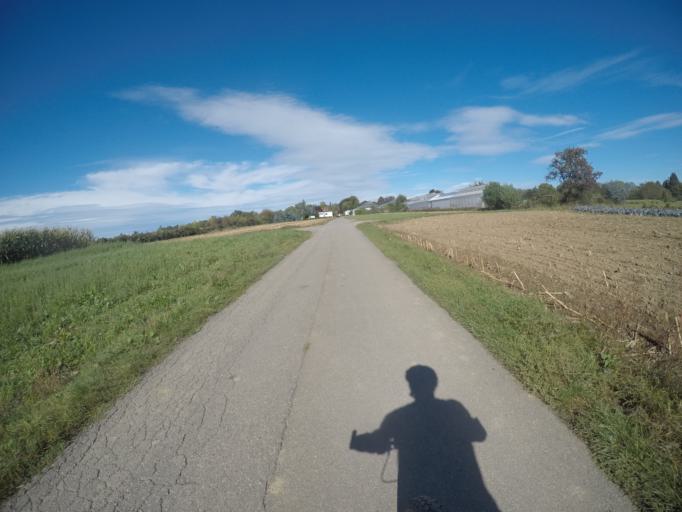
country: DE
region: Baden-Wuerttemberg
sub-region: Regierungsbezirk Stuttgart
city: Leinfelden-Echterdingen
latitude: 48.7364
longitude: 9.1578
